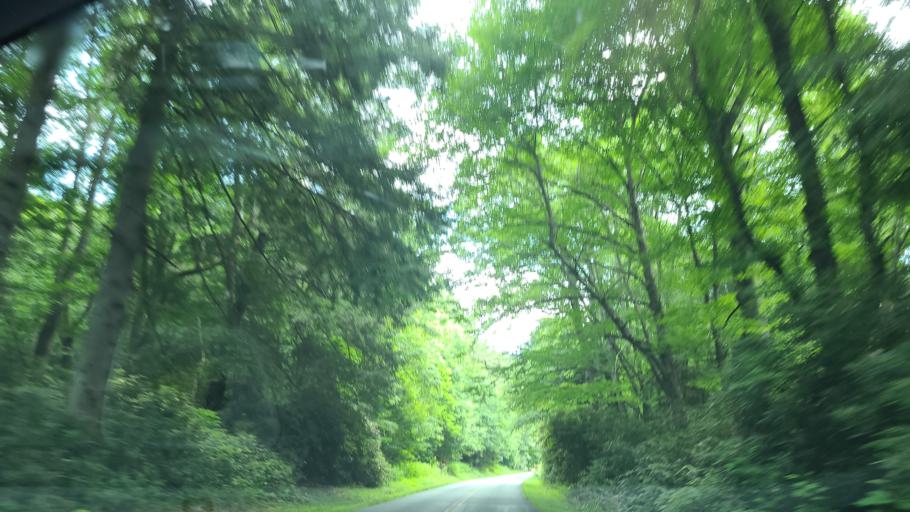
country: US
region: North Carolina
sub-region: Avery County
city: Newland
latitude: 35.9853
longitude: -81.9103
